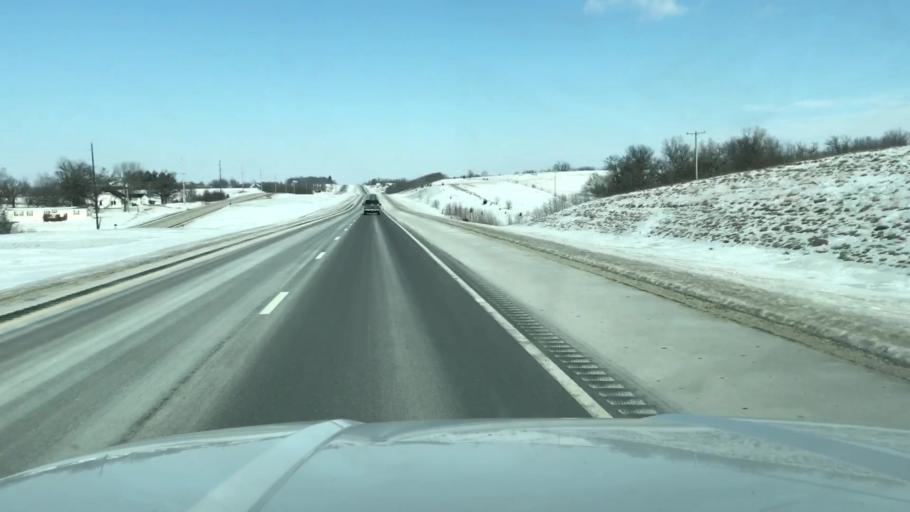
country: US
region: Missouri
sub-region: Nodaway County
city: Maryville
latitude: 40.1875
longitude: -94.8678
